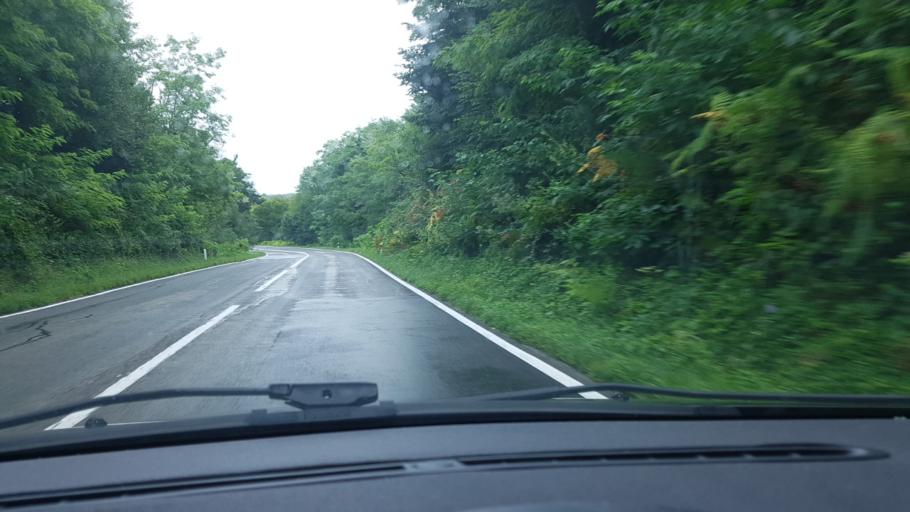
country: SI
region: Crnomelj
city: Crnomelj
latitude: 45.4470
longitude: 15.3257
